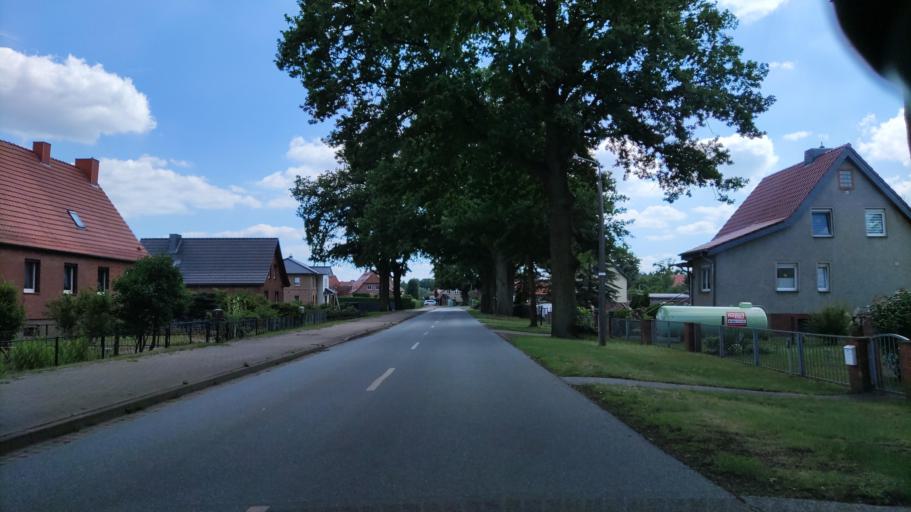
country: DE
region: Mecklenburg-Vorpommern
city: Lubtheen
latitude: 53.3388
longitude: 11.1426
